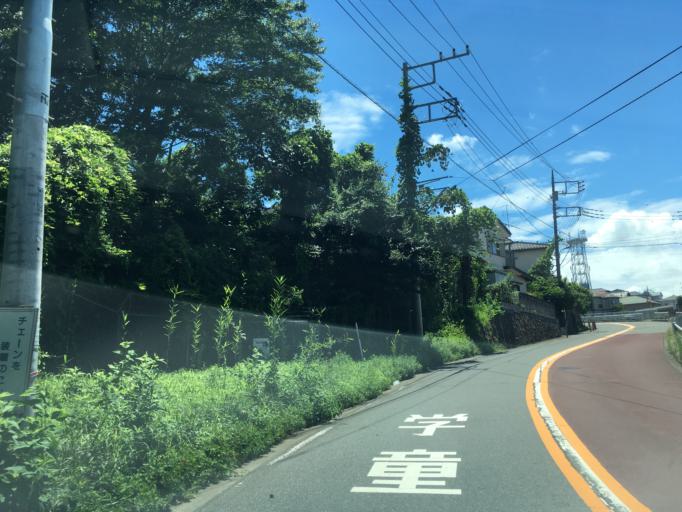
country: JP
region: Tokyo
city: Kokubunji
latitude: 35.6348
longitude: 139.4650
